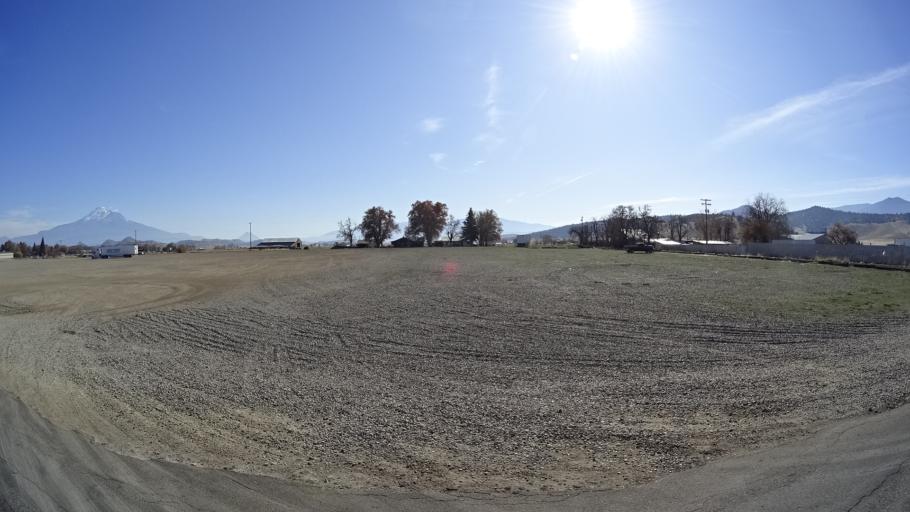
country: US
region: California
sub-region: Siskiyou County
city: Montague
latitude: 41.6472
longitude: -122.5308
